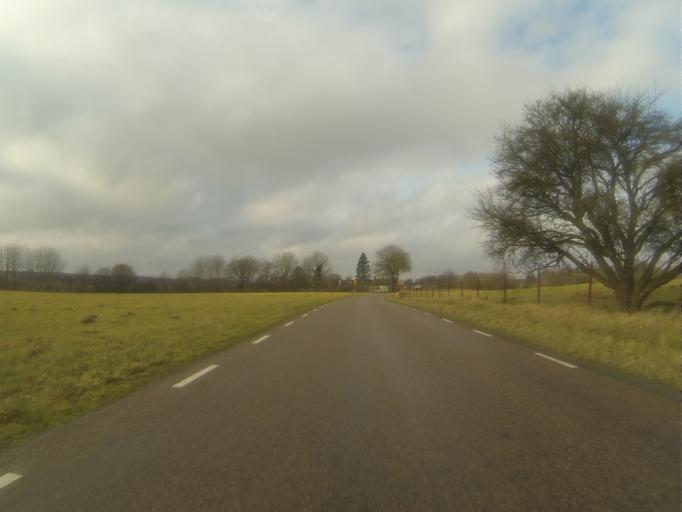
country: SE
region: Skane
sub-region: Svedala Kommun
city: Klagerup
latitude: 55.5678
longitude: 13.3103
